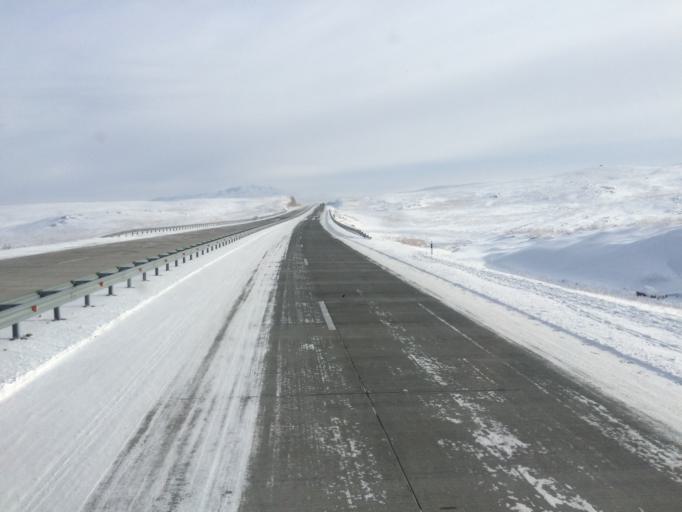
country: KZ
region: Zhambyl
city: Georgiyevka
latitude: 43.4217
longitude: 74.9682
